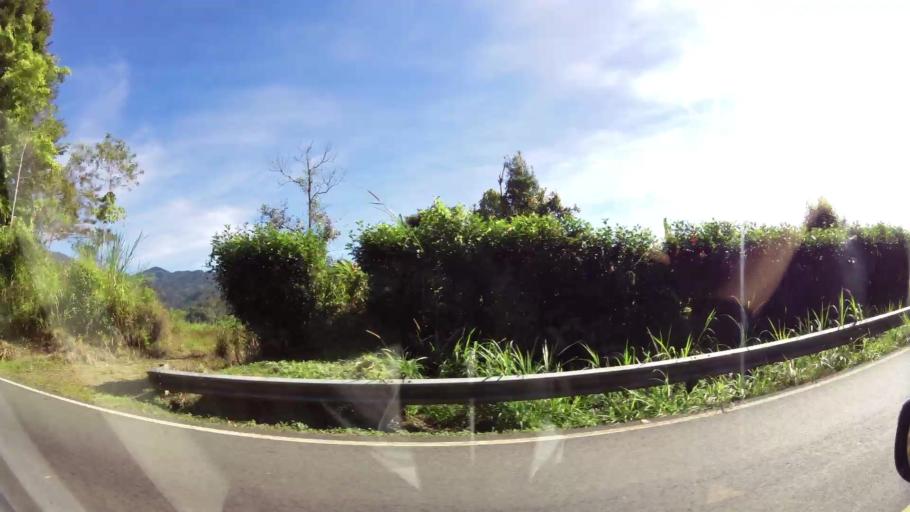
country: CR
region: San Jose
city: San Isidro
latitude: 9.4347
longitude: -83.7096
